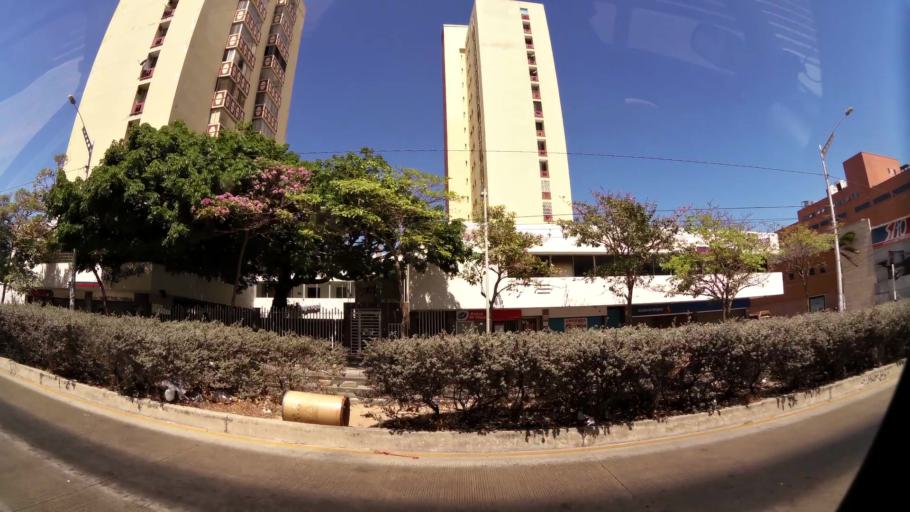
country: CO
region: Atlantico
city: Barranquilla
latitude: 10.9887
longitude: -74.7898
